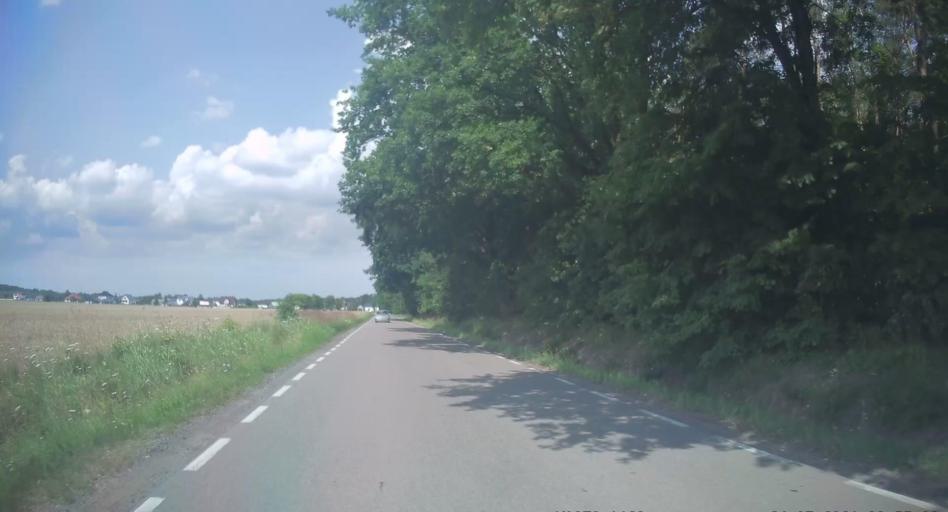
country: PL
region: Lodz Voivodeship
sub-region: Powiat tomaszowski
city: Lubochnia
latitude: 51.5746
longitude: 20.0785
